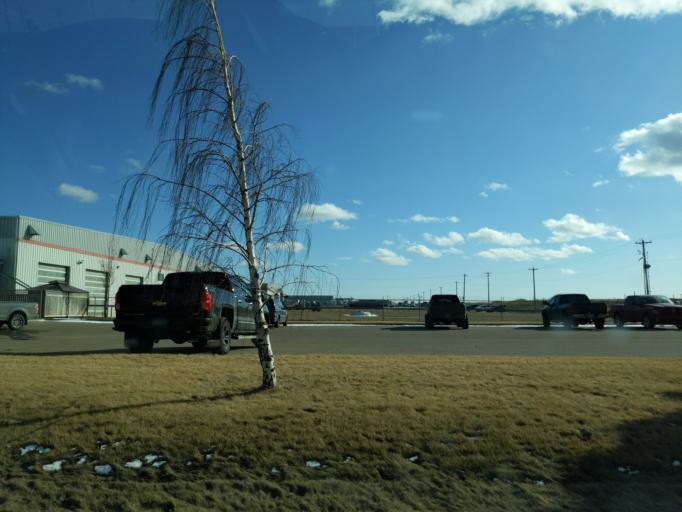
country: CA
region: Saskatchewan
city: Lloydminster
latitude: 53.2998
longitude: -110.0412
